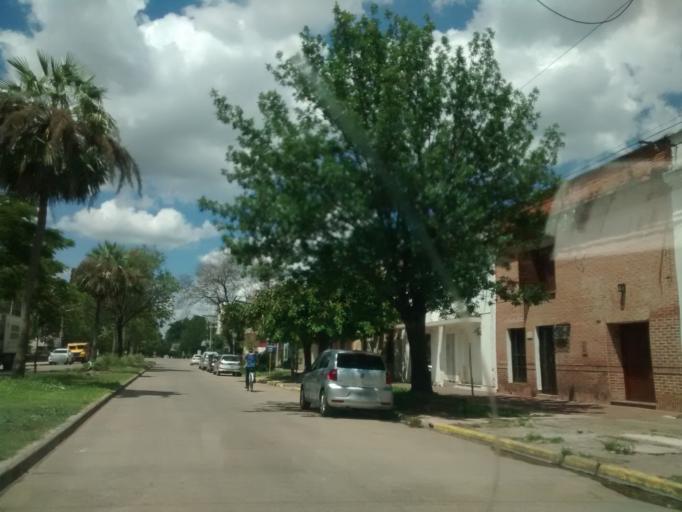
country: AR
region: Chaco
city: Resistencia
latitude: -27.4559
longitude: -58.9917
